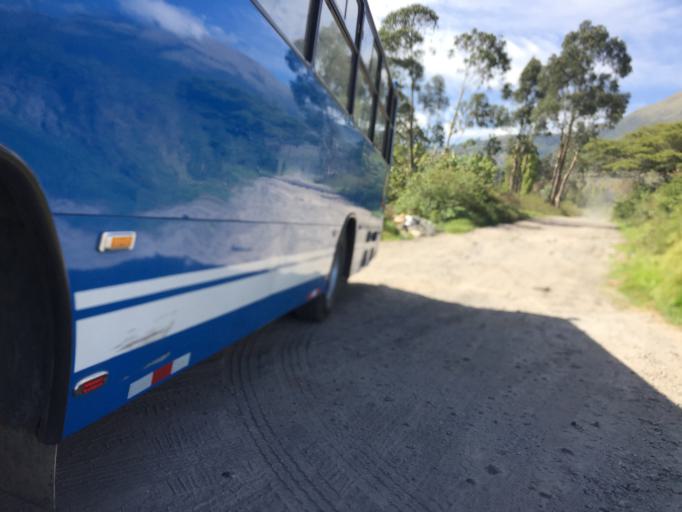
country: EC
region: Imbabura
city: Ibarra
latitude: 0.3170
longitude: -78.1475
